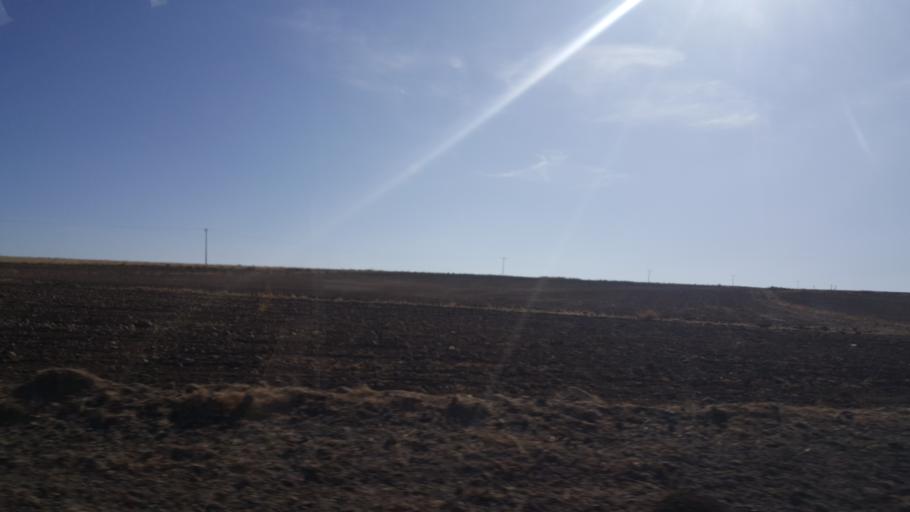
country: TR
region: Ankara
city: Altpinar
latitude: 39.2408
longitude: 32.7350
